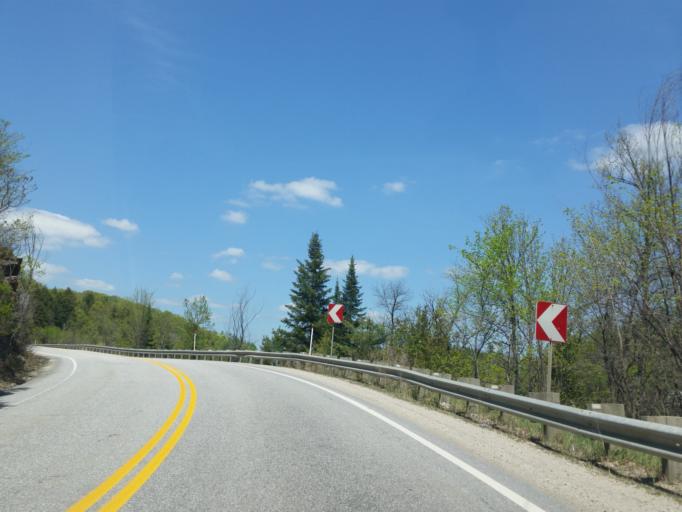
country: CA
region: Quebec
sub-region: Outaouais
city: Wakefield
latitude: 45.6530
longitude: -75.9248
